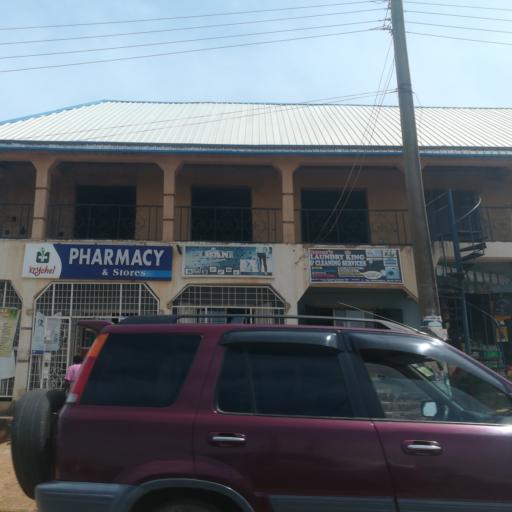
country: NG
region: Plateau
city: Jos
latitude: 9.8938
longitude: 8.8645
